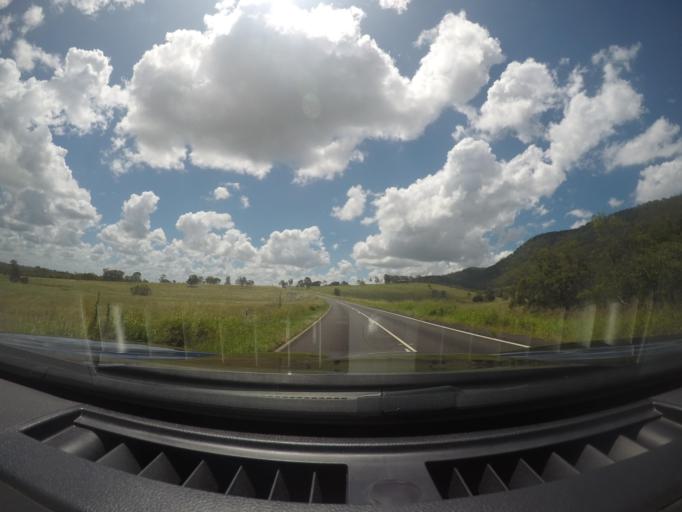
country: AU
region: Queensland
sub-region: Moreton Bay
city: Woodford
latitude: -27.1420
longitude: 152.5224
